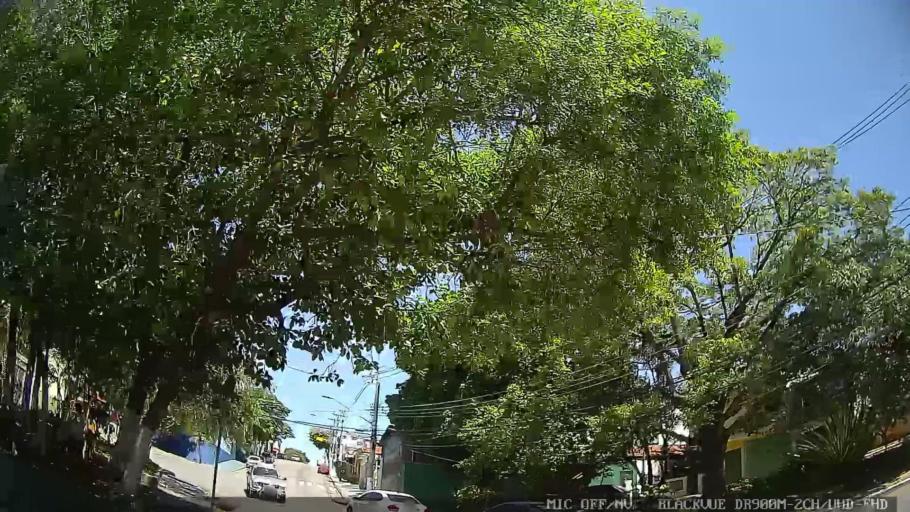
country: BR
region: Sao Paulo
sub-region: Sao Caetano Do Sul
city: Sao Caetano do Sul
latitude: -23.5899
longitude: -46.5311
